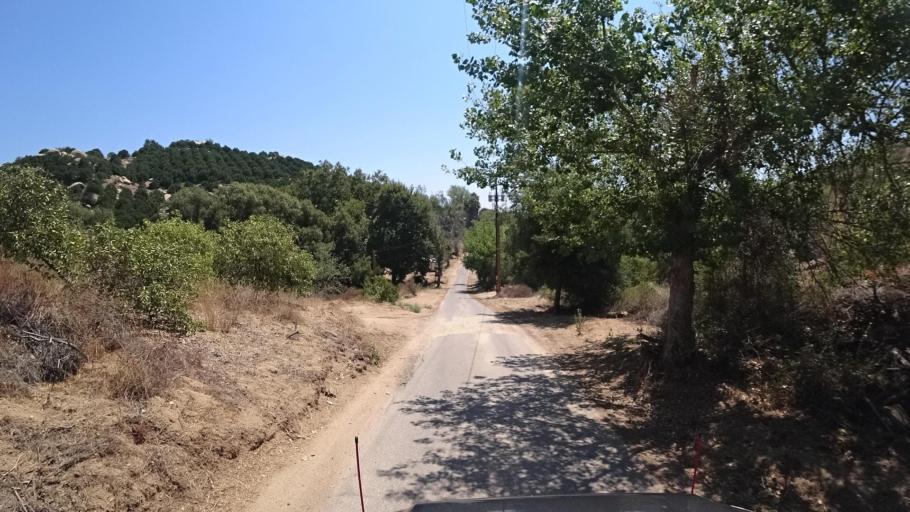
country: US
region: California
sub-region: San Diego County
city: Fallbrook
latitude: 33.4302
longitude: -117.2641
